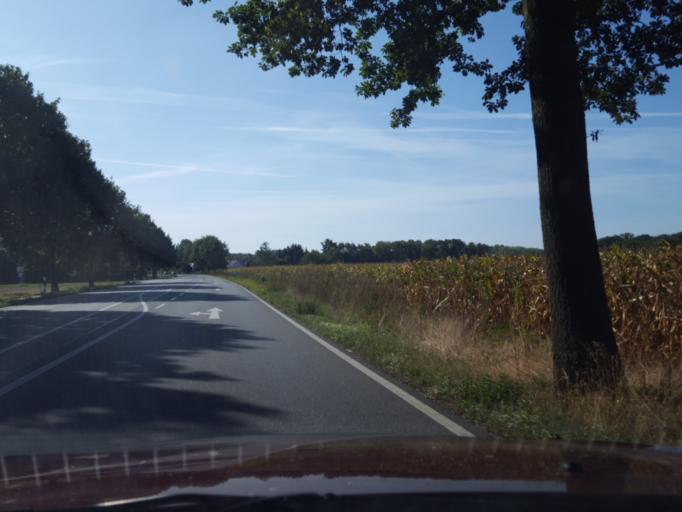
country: DE
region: Lower Saxony
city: Eystrup
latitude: 52.7876
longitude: 9.2115
